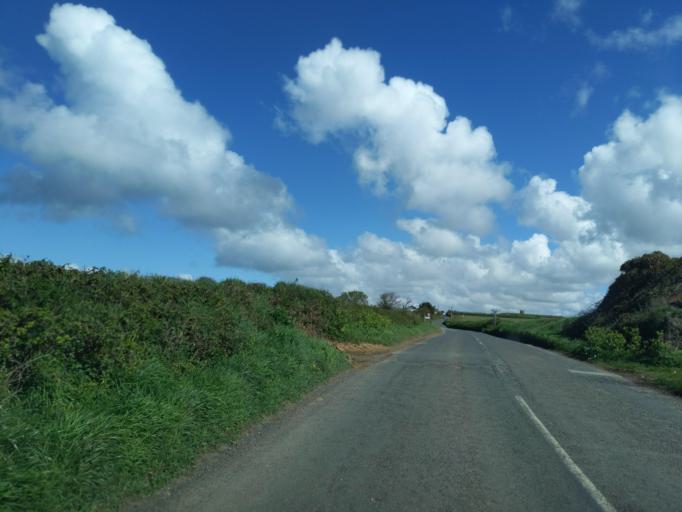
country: GB
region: England
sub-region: Cornwall
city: Wadebridge
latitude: 50.5739
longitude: -4.8410
